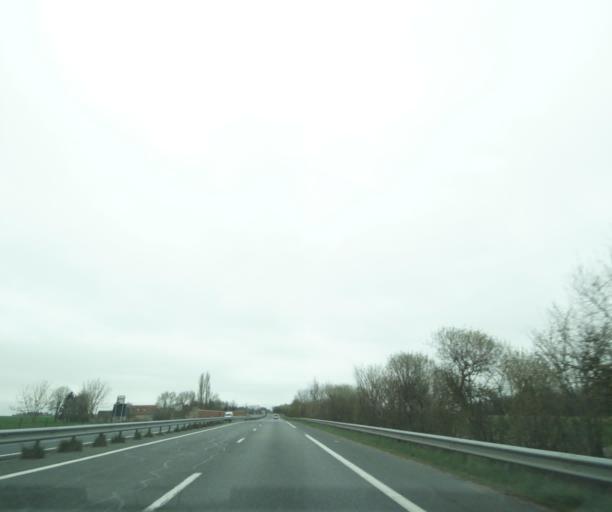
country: FR
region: Centre
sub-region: Departement de l'Indre
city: Vatan
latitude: 47.0853
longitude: 1.8348
